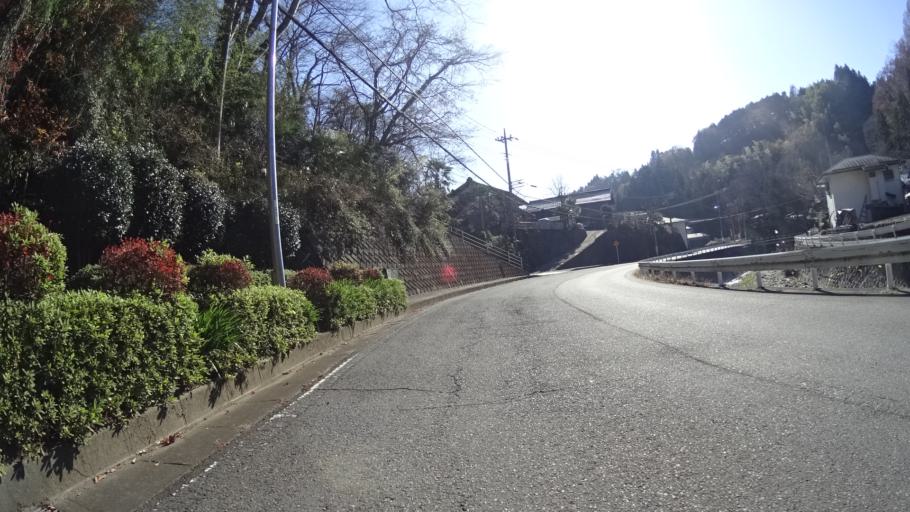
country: JP
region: Yamanashi
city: Uenohara
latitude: 35.6347
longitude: 139.1413
